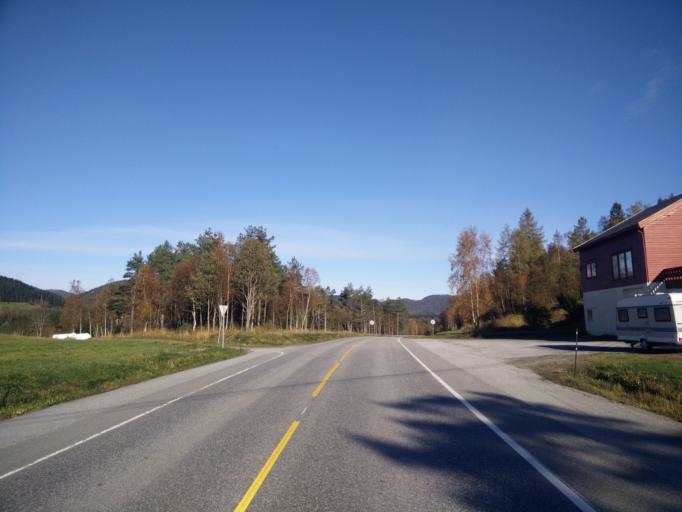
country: NO
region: More og Romsdal
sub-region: Kristiansund
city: Rensvik
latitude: 63.0229
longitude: 8.0153
